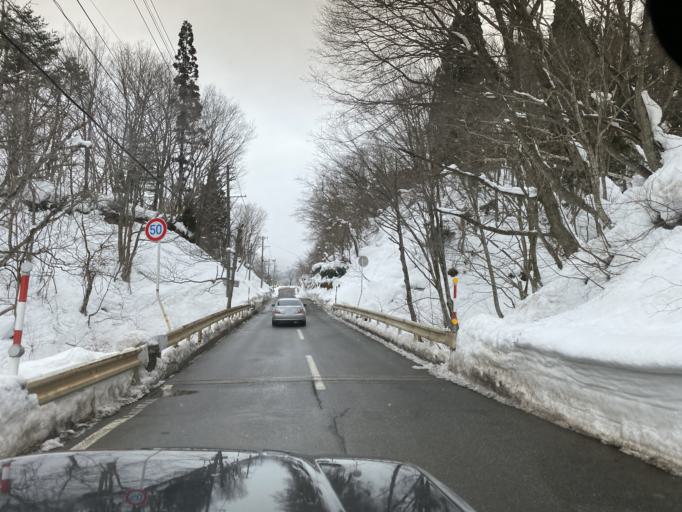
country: JP
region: Gifu
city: Takayama
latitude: 36.0985
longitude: 136.9343
